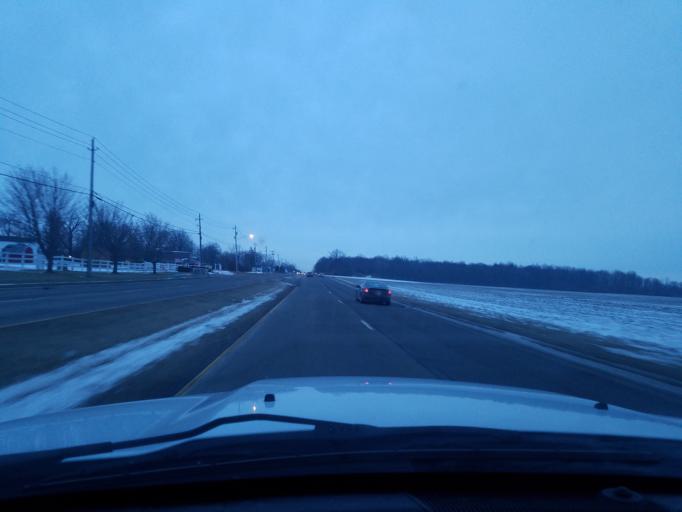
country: US
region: Indiana
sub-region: Delaware County
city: Muncie
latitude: 40.2190
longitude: -85.3578
